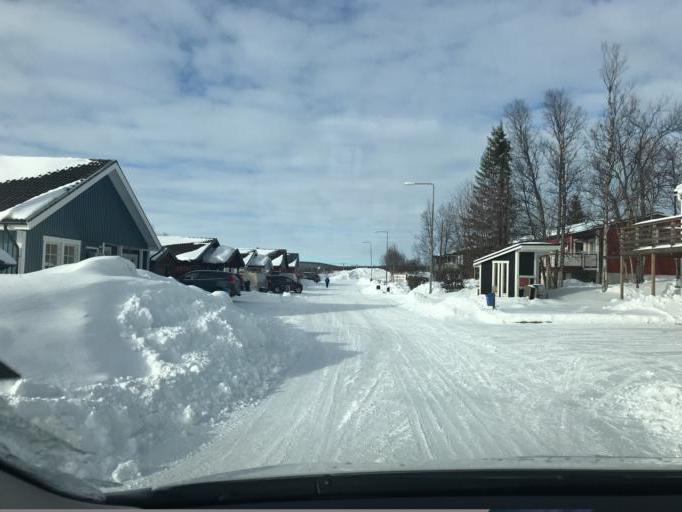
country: SE
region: Norrbotten
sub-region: Kiruna Kommun
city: Kiruna
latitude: 67.8664
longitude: 20.2053
